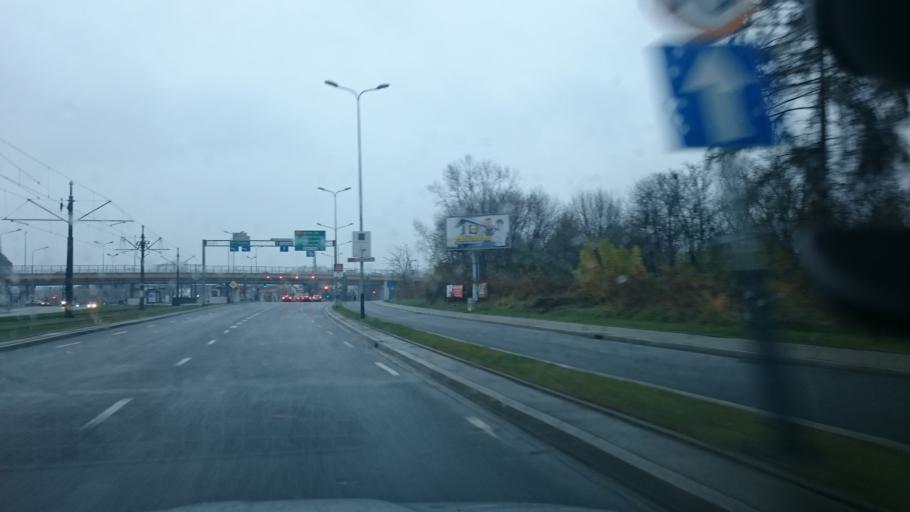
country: PL
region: Lesser Poland Voivodeship
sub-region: Krakow
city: Krakow
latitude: 50.0434
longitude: 19.9743
